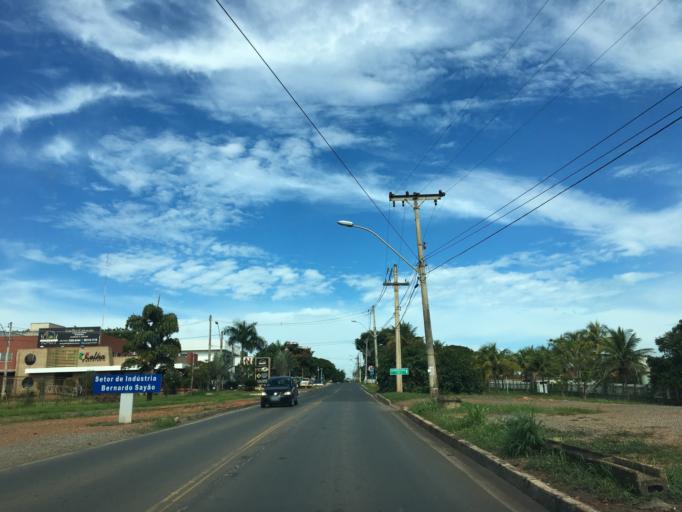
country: BR
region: Federal District
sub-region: Brasilia
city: Brasilia
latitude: -15.8653
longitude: -47.9650
